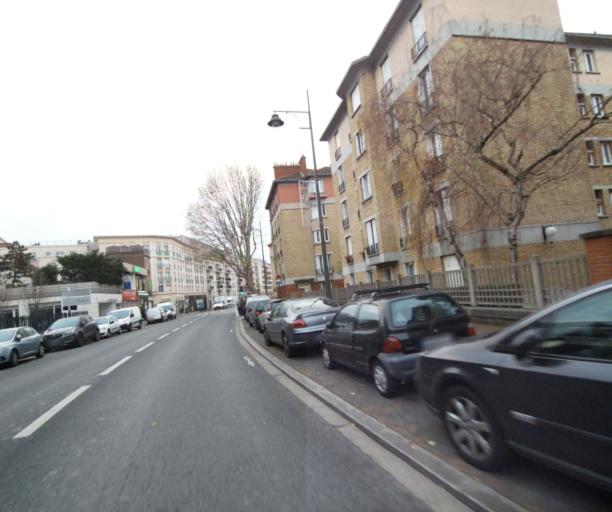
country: FR
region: Ile-de-France
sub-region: Departement des Hauts-de-Seine
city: Saint-Cloud
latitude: 48.8646
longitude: 2.2074
